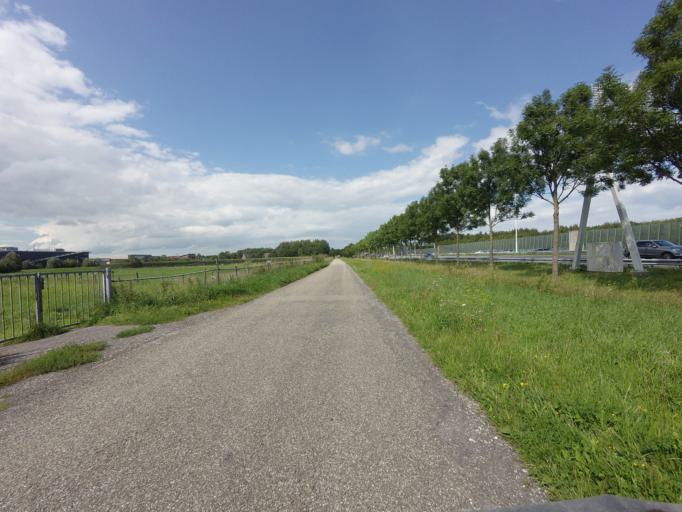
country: NL
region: Utrecht
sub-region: Gemeente Nieuwegein
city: Nieuwegein
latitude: 52.0110
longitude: 5.0706
